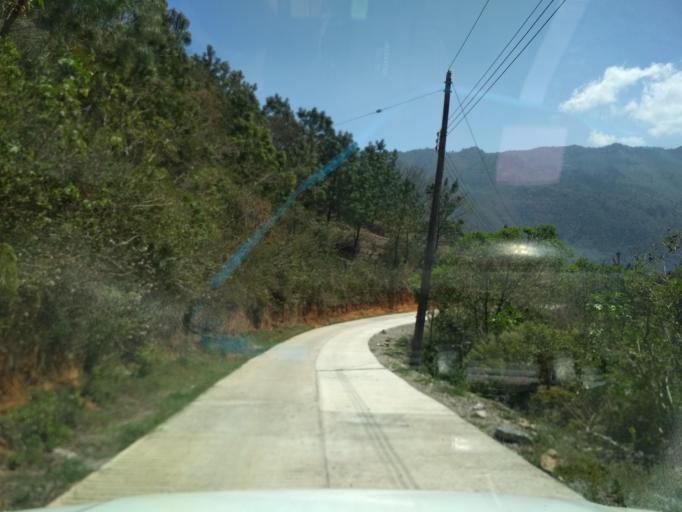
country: MX
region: Veracruz
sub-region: Tlilapan
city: Tonalixco
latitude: 18.7748
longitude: -97.0876
